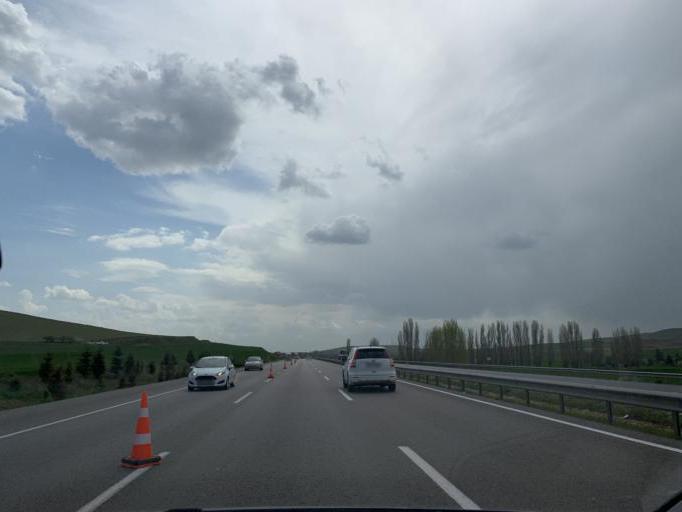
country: TR
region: Ankara
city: Polatli
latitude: 39.6372
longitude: 32.2022
